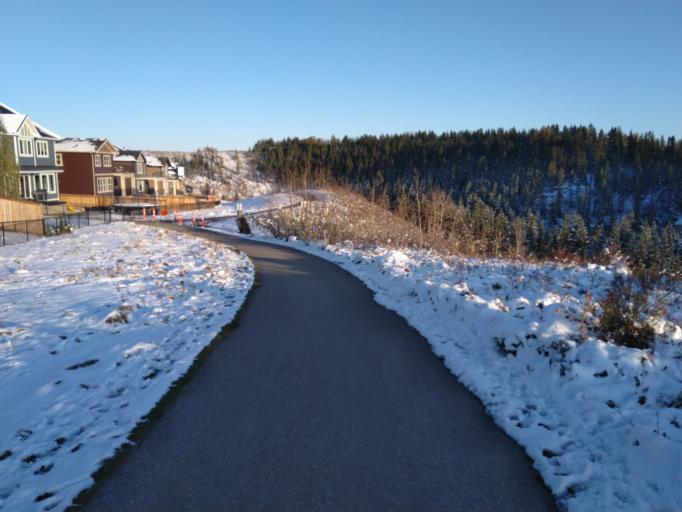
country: CA
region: Alberta
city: Cochrane
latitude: 51.1812
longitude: -114.5051
